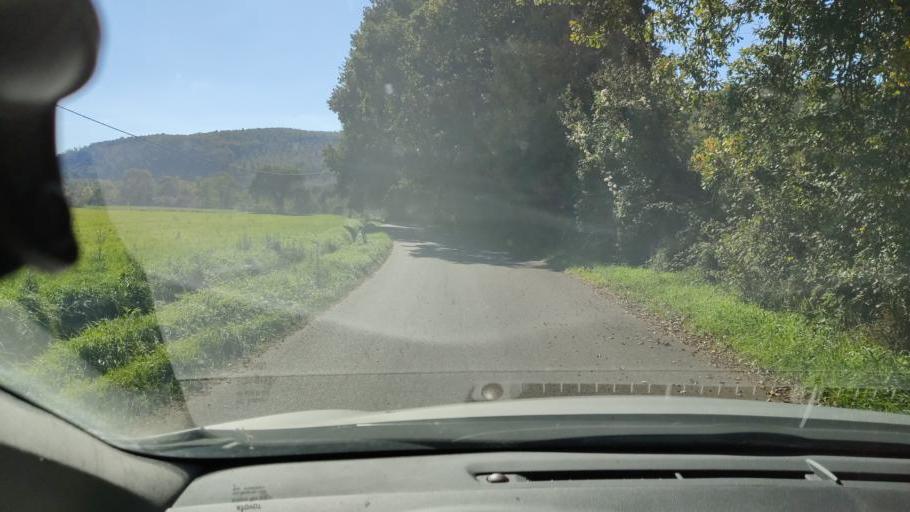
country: IT
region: Umbria
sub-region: Provincia di Terni
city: Amelia
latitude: 42.5928
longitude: 12.4357
